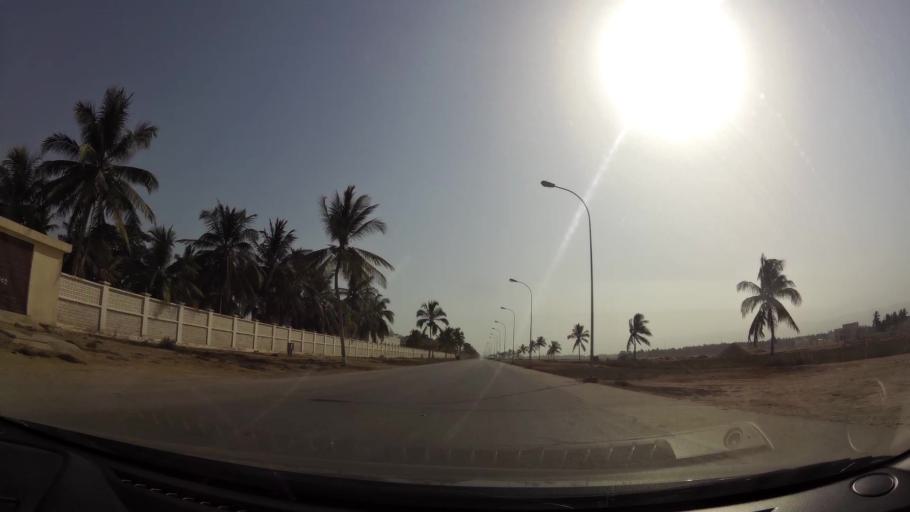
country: OM
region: Zufar
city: Salalah
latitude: 16.9964
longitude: 54.0649
